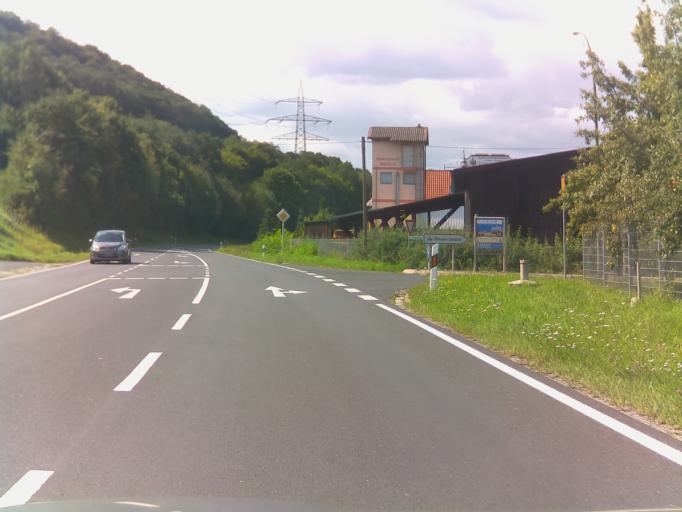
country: DE
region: Bavaria
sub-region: Regierungsbezirk Unterfranken
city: Eltmann
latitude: 49.9783
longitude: 10.6425
